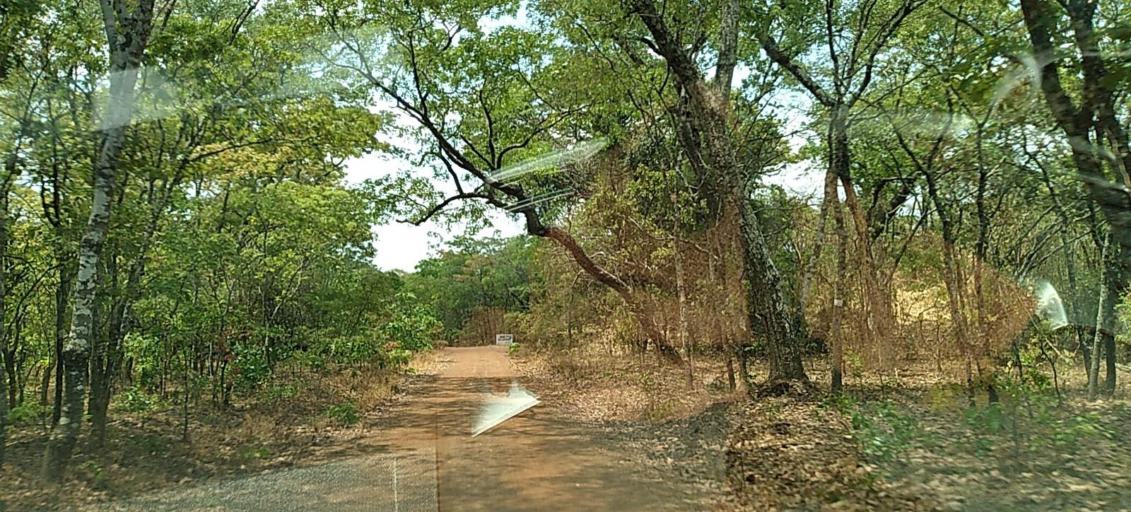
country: ZM
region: Copperbelt
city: Chililabombwe
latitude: -12.4987
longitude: 27.6407
